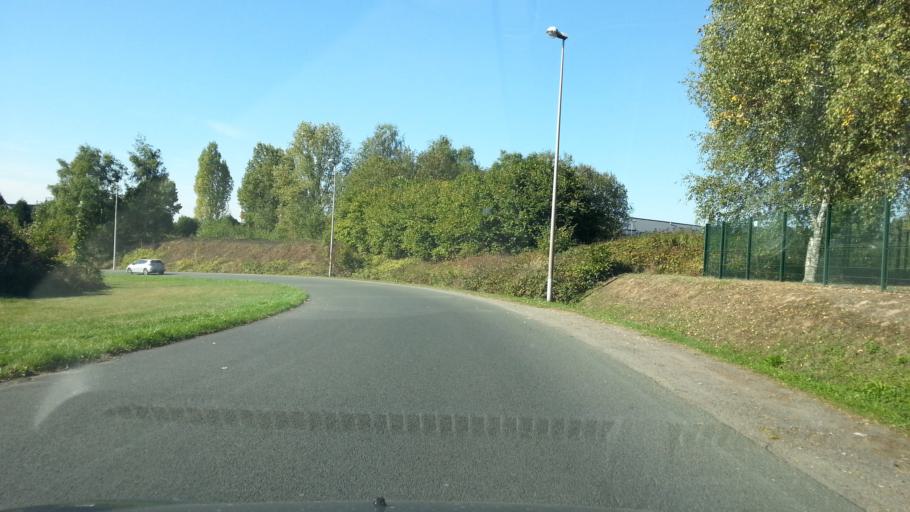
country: FR
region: Picardie
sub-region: Departement de l'Oise
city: Creil
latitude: 49.2465
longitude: 2.4703
